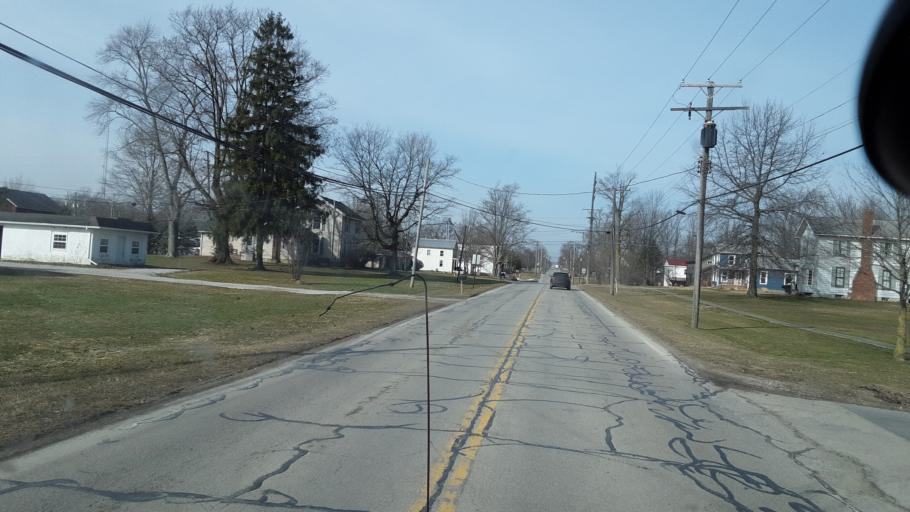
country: US
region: Ohio
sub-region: Ashtabula County
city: Jefferson
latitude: 41.7384
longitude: -80.7578
